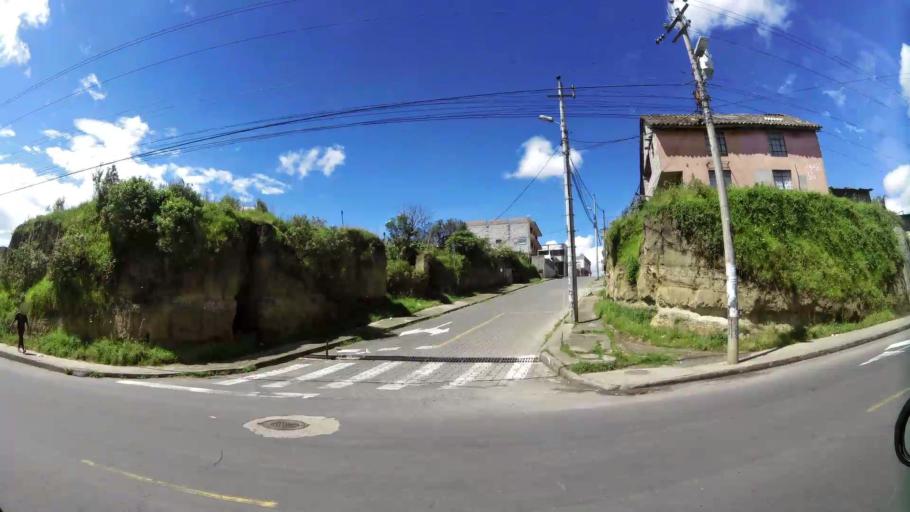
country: EC
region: Pichincha
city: Quito
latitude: -0.3153
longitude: -78.5608
